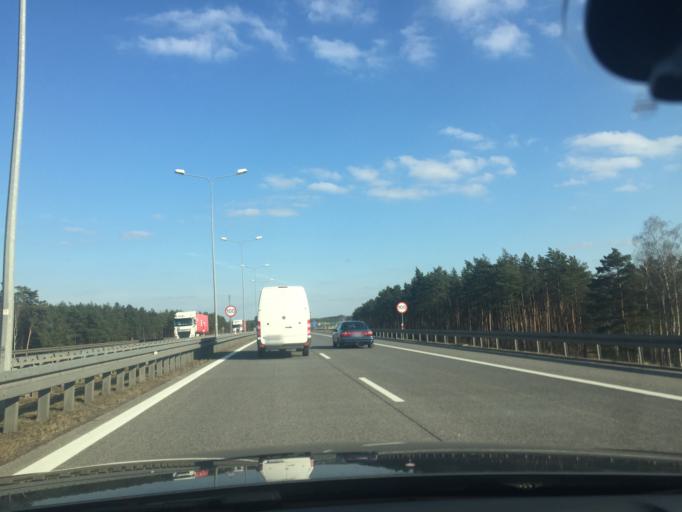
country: PL
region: Lubusz
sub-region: Powiat slubicki
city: Rzepin
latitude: 52.3349
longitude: 14.8923
